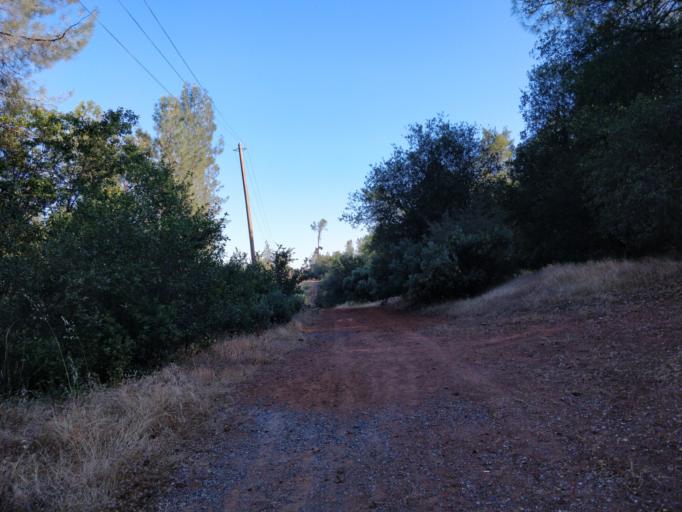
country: US
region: California
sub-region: Shasta County
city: Shasta Lake
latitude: 40.6727
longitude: -122.3614
